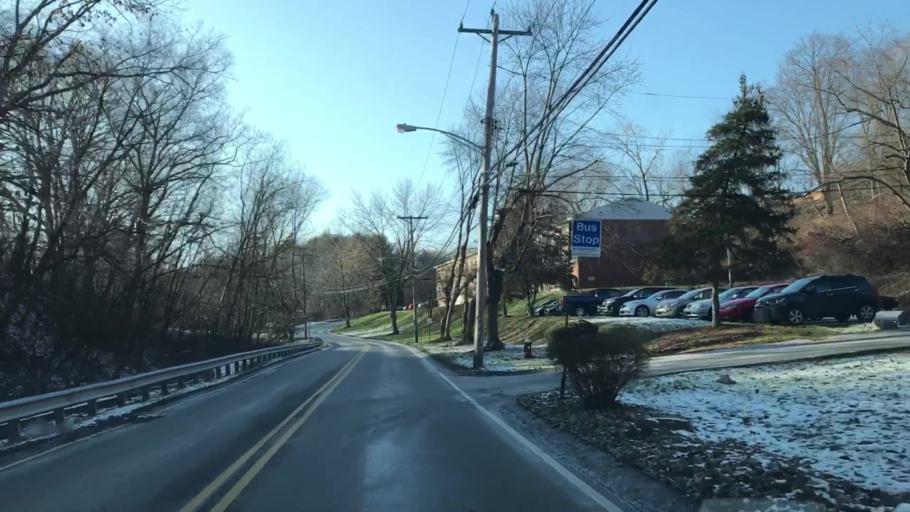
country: US
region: Pennsylvania
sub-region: Allegheny County
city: Allison Park
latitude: 40.5822
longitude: -79.9951
